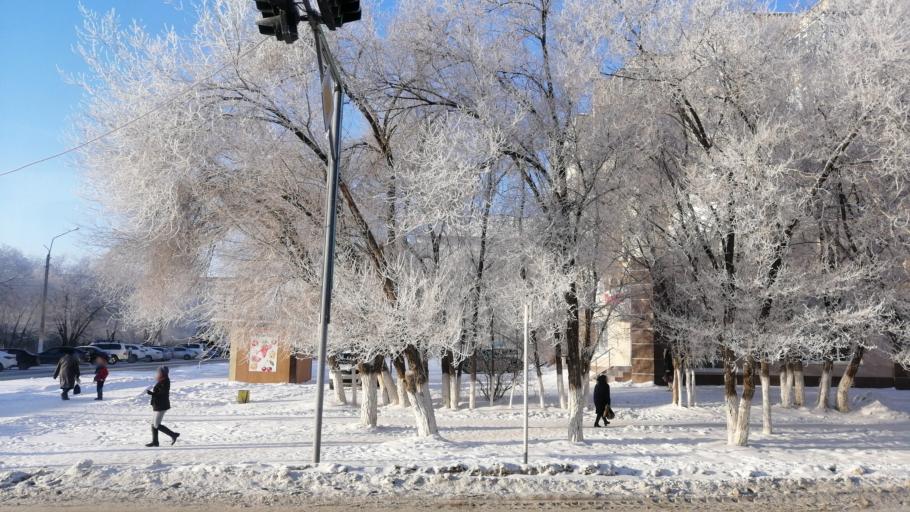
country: KZ
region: Aqtoebe
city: Aqtobe
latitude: 50.2923
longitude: 57.1497
